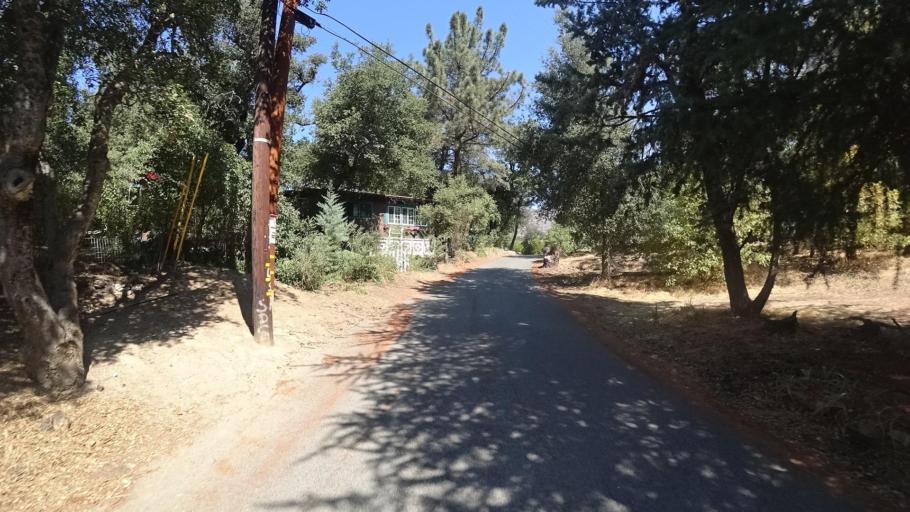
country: US
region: California
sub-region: San Diego County
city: Julian
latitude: 33.0849
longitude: -116.5874
